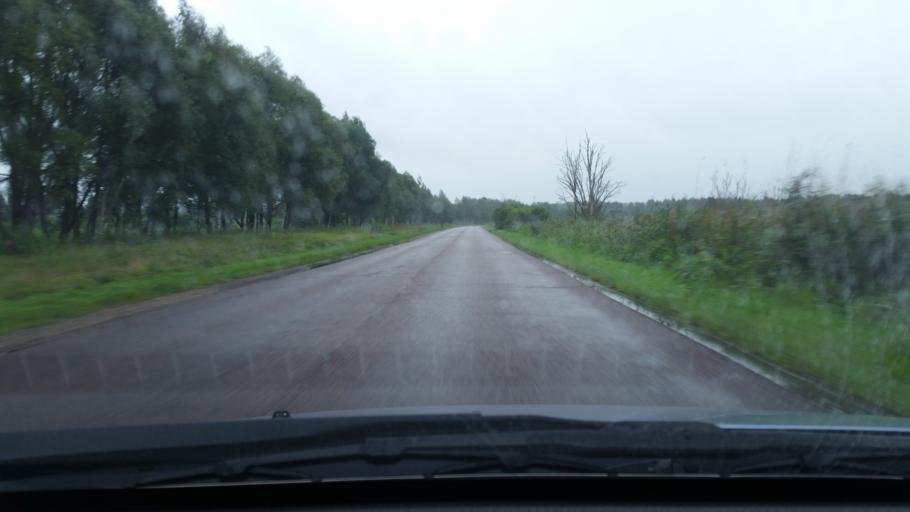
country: LV
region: Riga
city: Bolderaja
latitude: 56.9940
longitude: 24.0306
